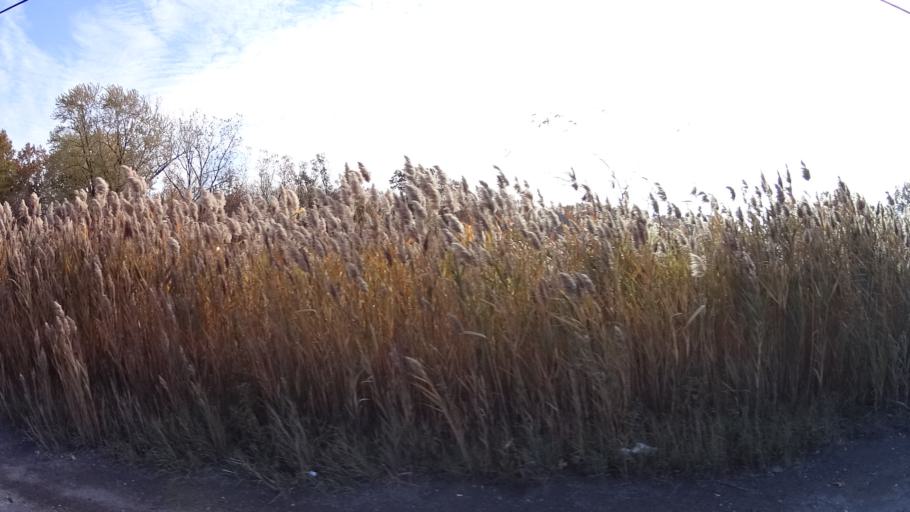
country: US
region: Ohio
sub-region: Lorain County
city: Lorain
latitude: 41.4631
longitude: -82.1573
